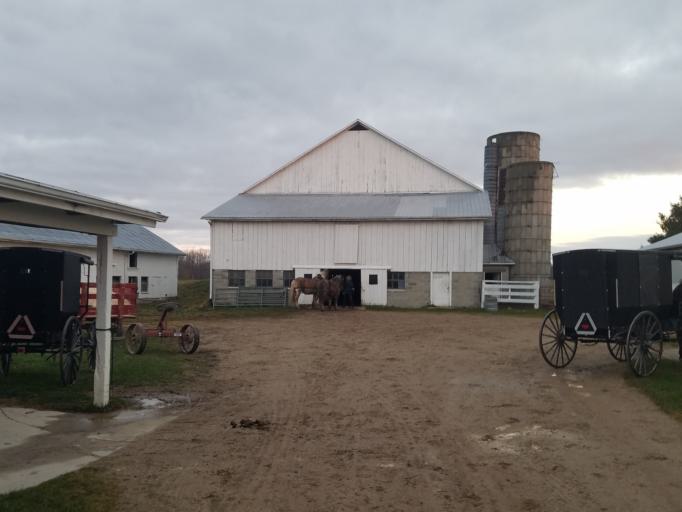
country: US
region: Michigan
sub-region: Mecosta County
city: Canadian Lakes
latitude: 43.5692
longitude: -85.3727
